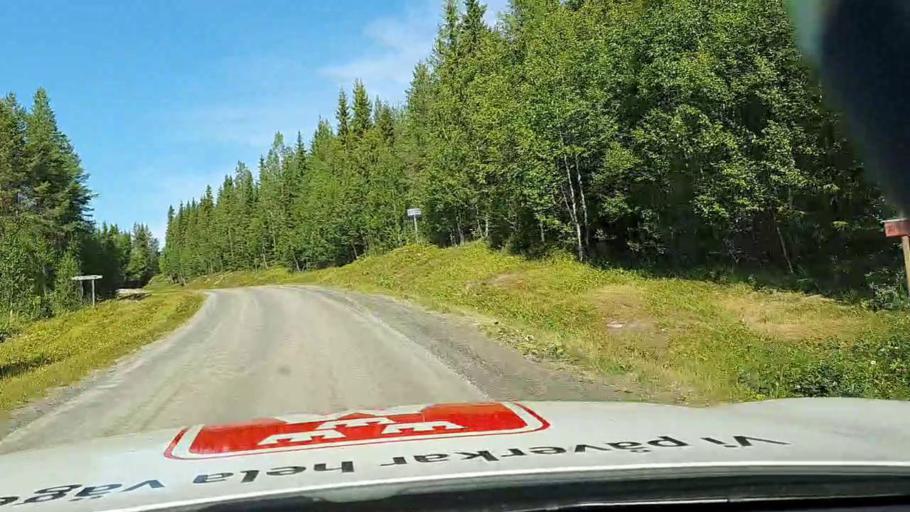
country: SE
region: Jaemtland
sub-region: Krokoms Kommun
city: Valla
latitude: 64.0908
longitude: 14.1394
